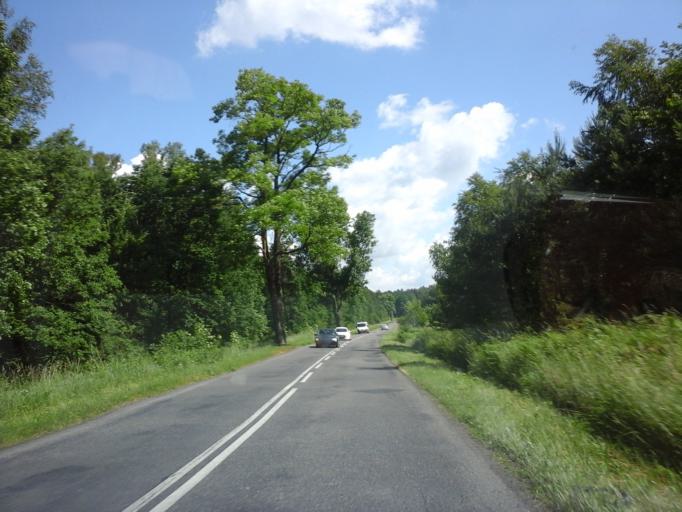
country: PL
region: West Pomeranian Voivodeship
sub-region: Powiat lobeski
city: Lobez
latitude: 53.6621
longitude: 15.6518
